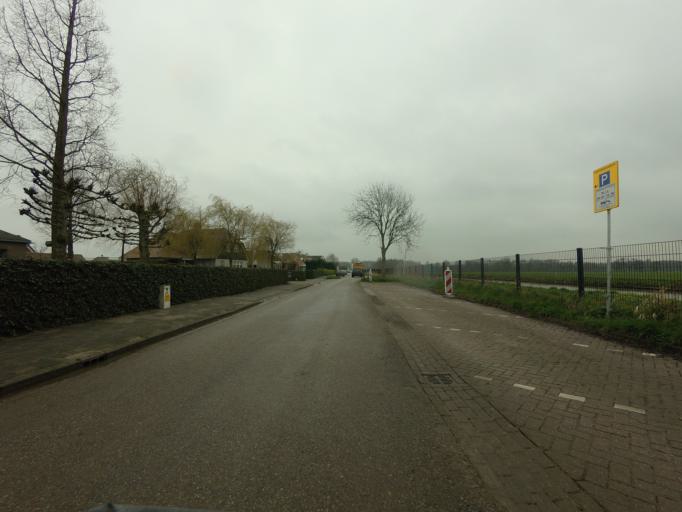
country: NL
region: Utrecht
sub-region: Stichtse Vecht
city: Breukelen
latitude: 52.1812
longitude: 5.0196
